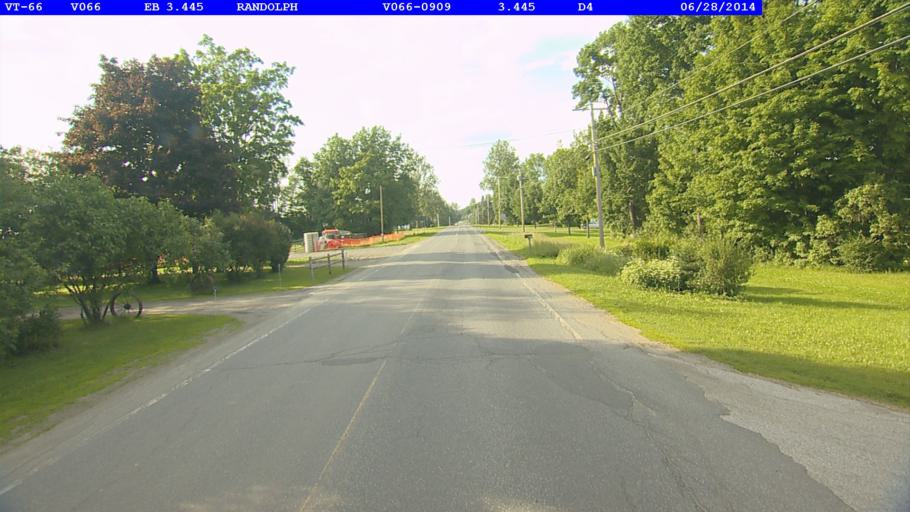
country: US
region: Vermont
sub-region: Orange County
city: Randolph
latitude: 43.9422
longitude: -72.6073
